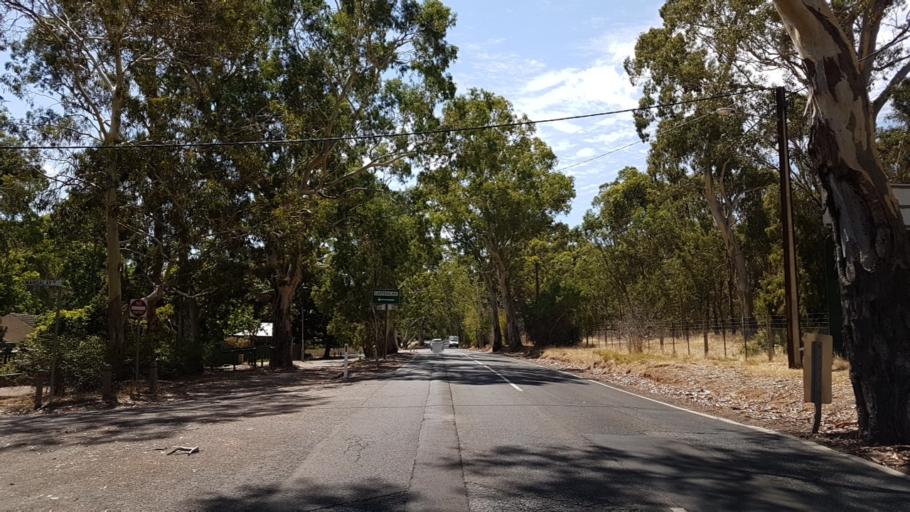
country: AU
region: South Australia
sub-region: Mitcham
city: Belair
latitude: -35.0069
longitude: 138.6331
